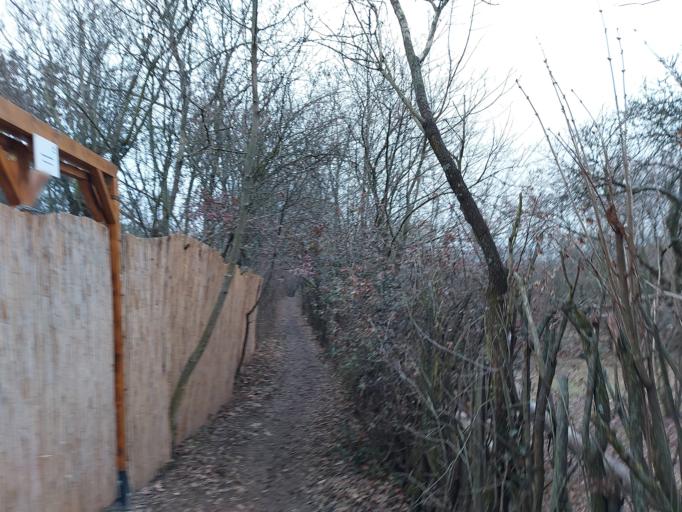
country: HU
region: Budapest
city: Budapest XII. keruelet
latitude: 47.4786
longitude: 19.0147
